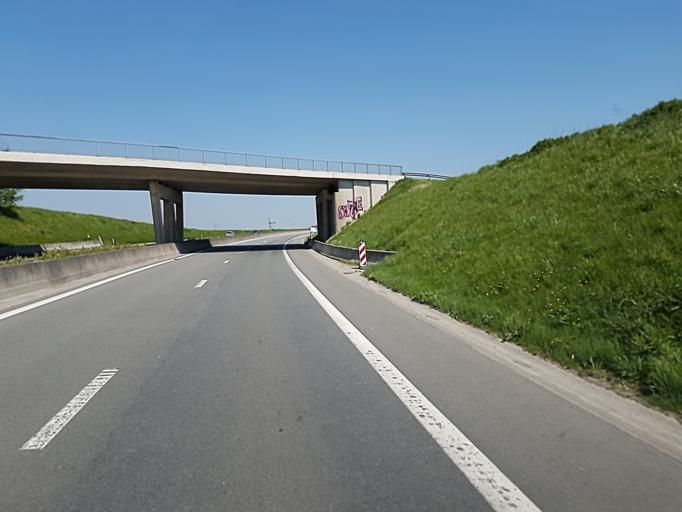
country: BE
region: Wallonia
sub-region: Province du Brabant Wallon
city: Nivelles
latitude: 50.5986
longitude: 4.3817
